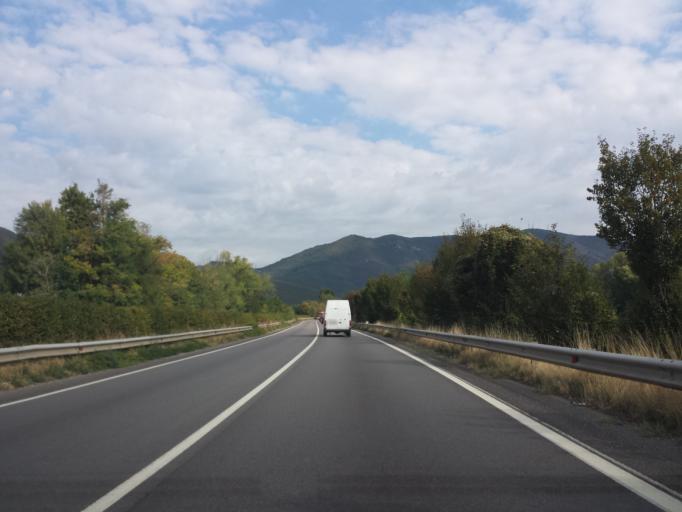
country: IT
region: Lombardy
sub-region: Provincia di Brescia
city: Gavardo-Sopraponte
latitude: 45.5691
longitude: 10.4421
